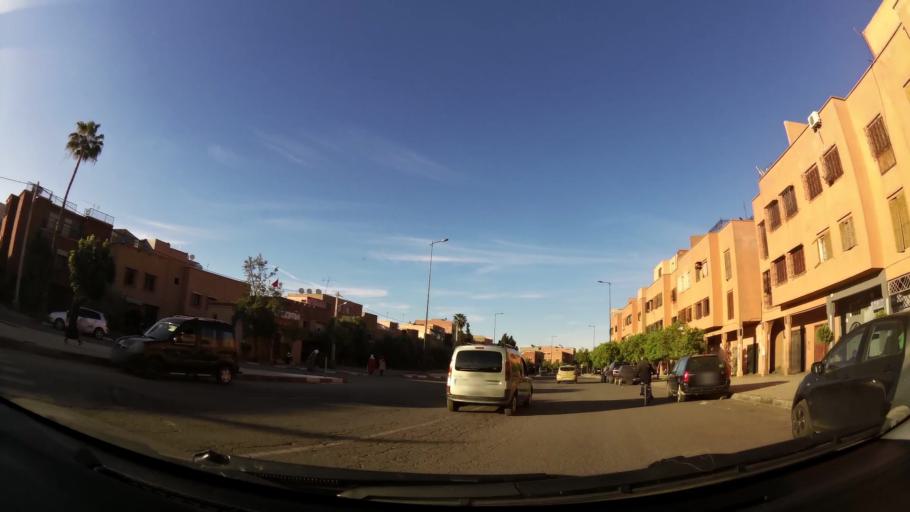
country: MA
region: Marrakech-Tensift-Al Haouz
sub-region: Marrakech
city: Marrakesh
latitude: 31.6206
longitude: -8.0576
